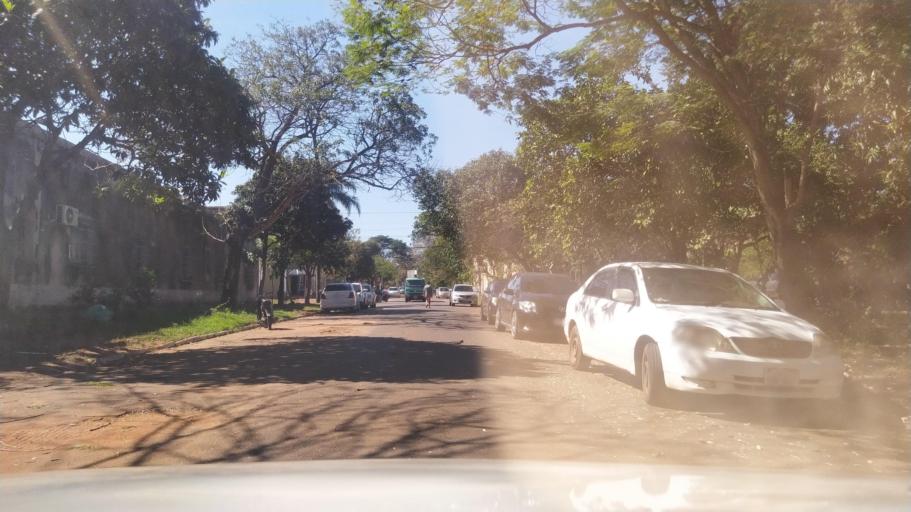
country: PY
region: Misiones
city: San Juan Bautista
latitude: -26.6667
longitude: -57.1506
